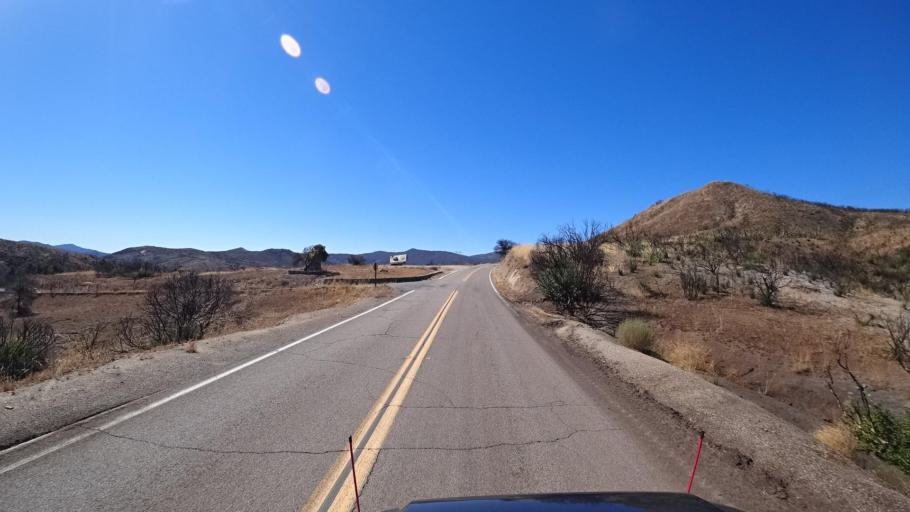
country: US
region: California
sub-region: San Diego County
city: Alpine
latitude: 32.7300
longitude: -116.6943
